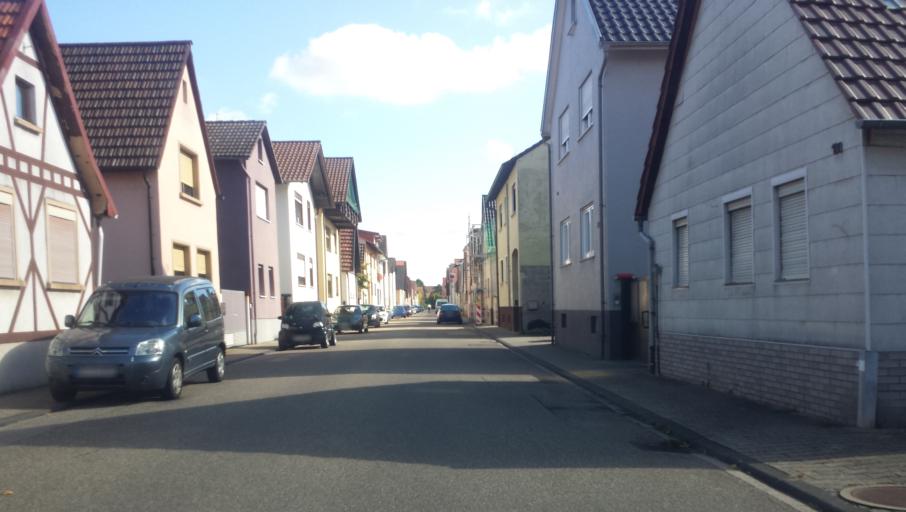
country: DE
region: Baden-Wuerttemberg
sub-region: Karlsruhe Region
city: Waghausel
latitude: 49.2376
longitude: 8.5494
